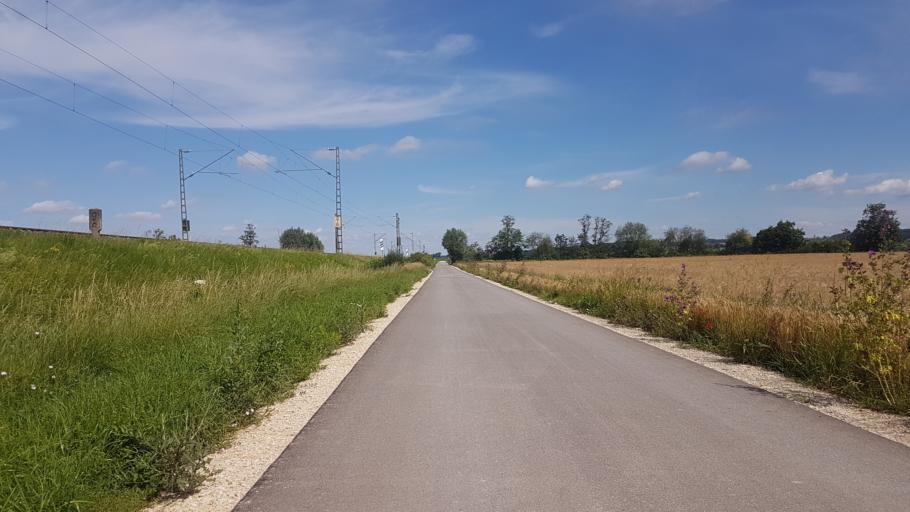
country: DE
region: Bavaria
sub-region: Regierungsbezirk Mittelfranken
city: Markt Berolzheim
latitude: 49.0300
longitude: 10.8437
